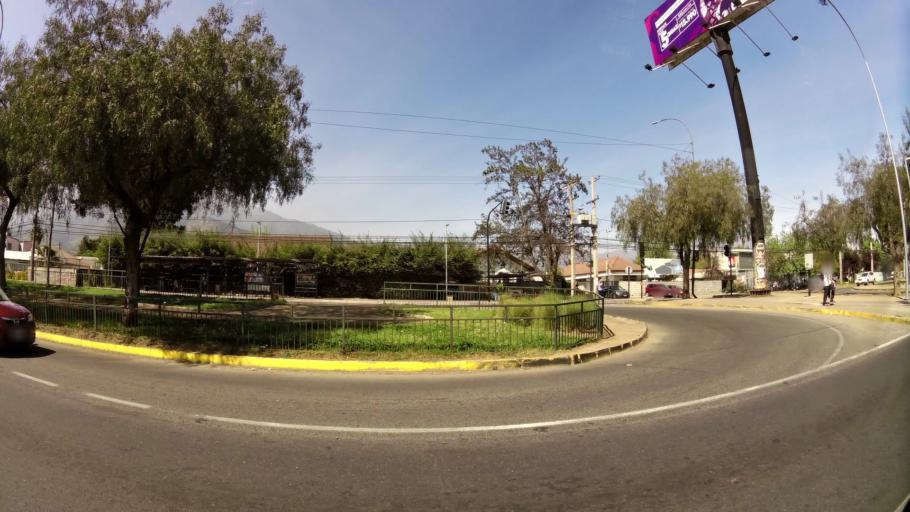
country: CL
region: Santiago Metropolitan
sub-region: Provincia de Cordillera
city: Puente Alto
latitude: -33.5693
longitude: -70.5548
